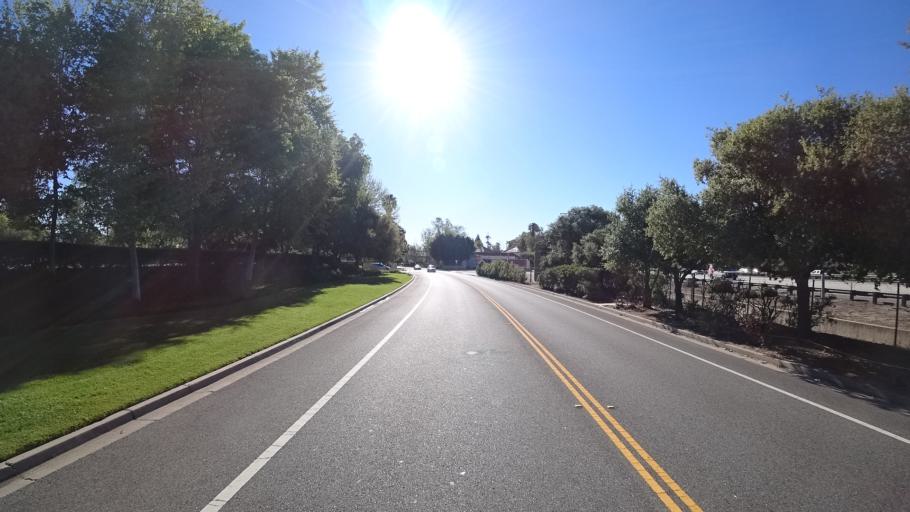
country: US
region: California
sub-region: Ventura County
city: Casa Conejo
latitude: 34.1866
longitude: -118.9308
